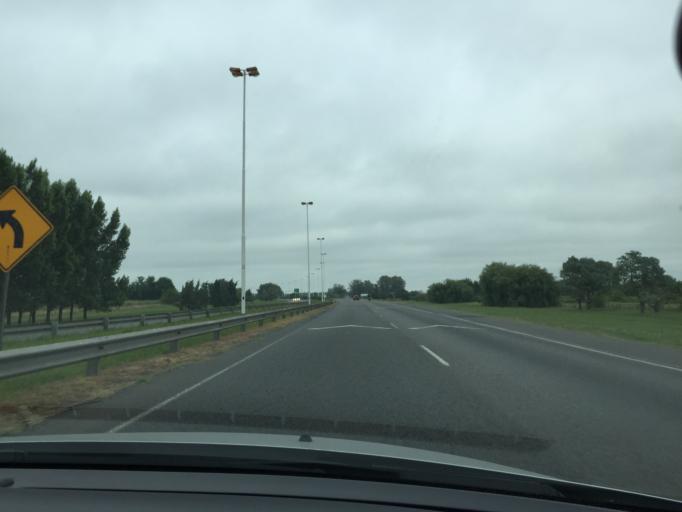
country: AR
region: Buenos Aires
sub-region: Partido de Ezeiza
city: Ezeiza
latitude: -34.8635
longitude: -58.5705
